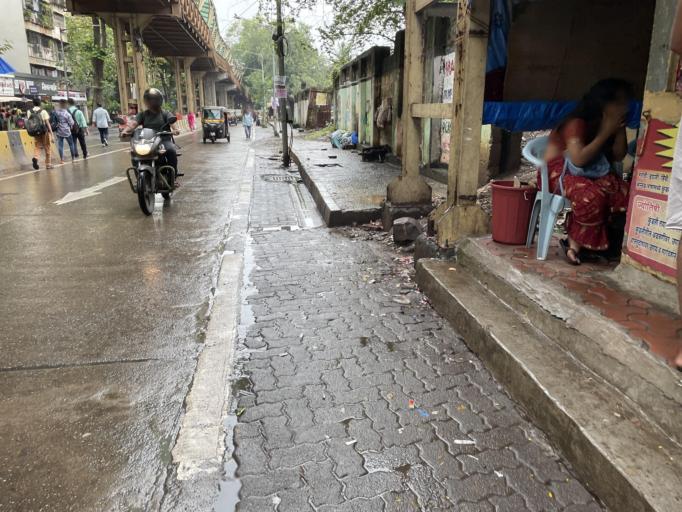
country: IN
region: Maharashtra
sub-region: Mumbai Suburban
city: Borivli
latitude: 19.2510
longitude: 72.8592
